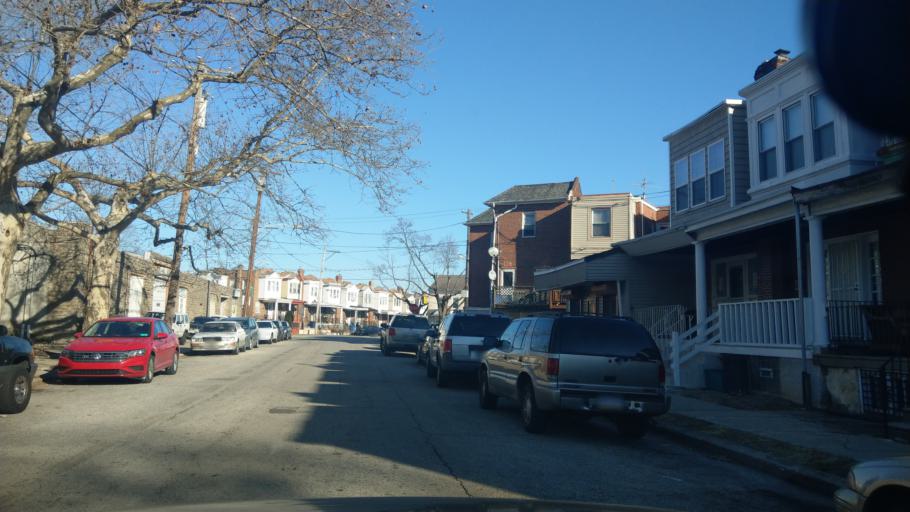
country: US
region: Pennsylvania
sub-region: Montgomery County
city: Wyncote
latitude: 40.0573
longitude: -75.1533
